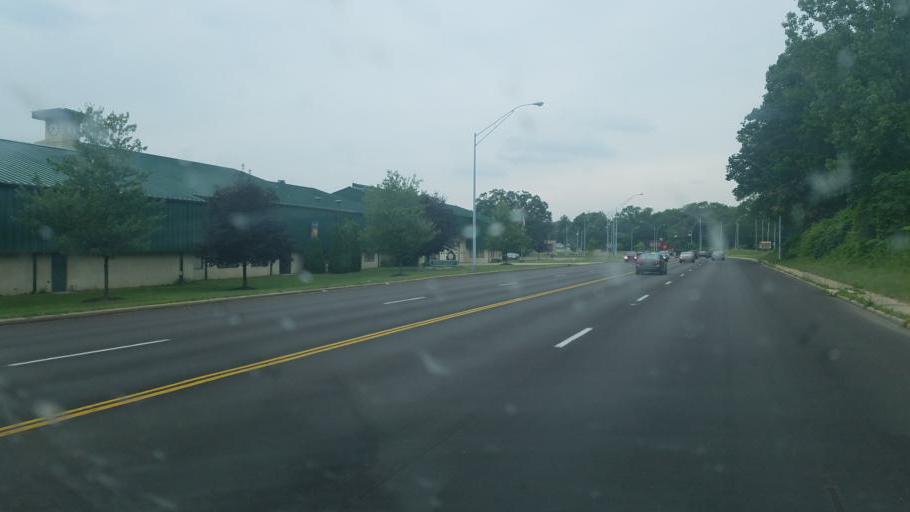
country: US
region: Ohio
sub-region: Summit County
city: Sawyerwood
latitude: 41.0346
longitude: -81.4398
